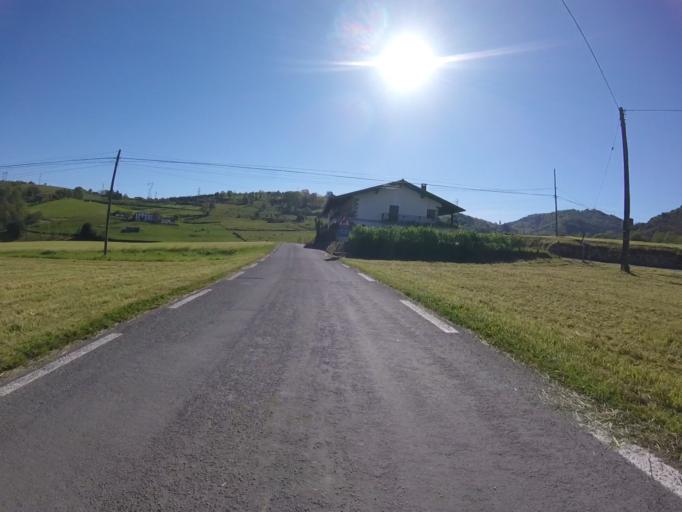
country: ES
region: Basque Country
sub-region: Provincia de Guipuzcoa
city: Aizarnazabal
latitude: 43.2331
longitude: -2.2242
